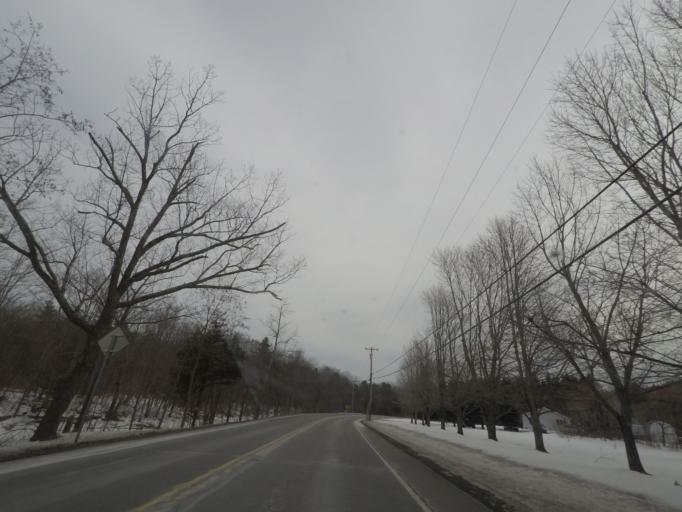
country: US
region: New York
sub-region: Albany County
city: Voorheesville
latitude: 42.5903
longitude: -73.9841
